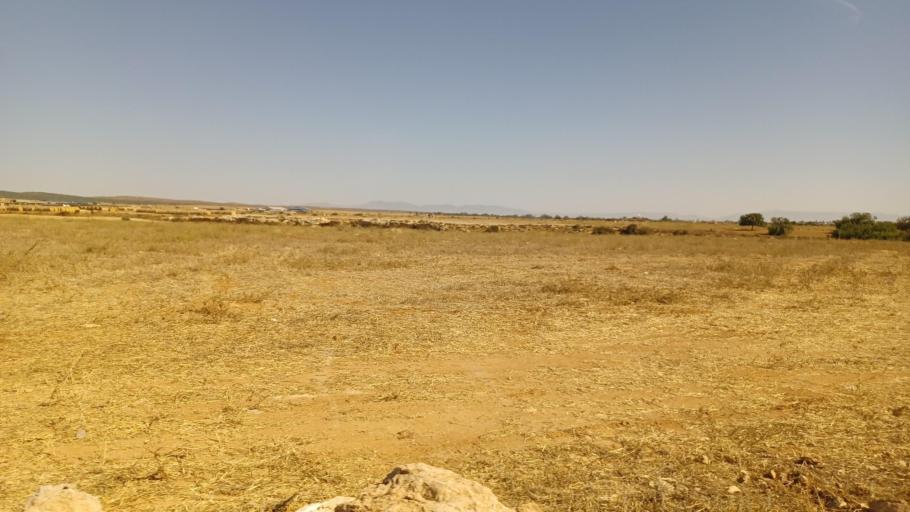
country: CY
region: Larnaka
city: Pyla
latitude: 35.0216
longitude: 33.6996
